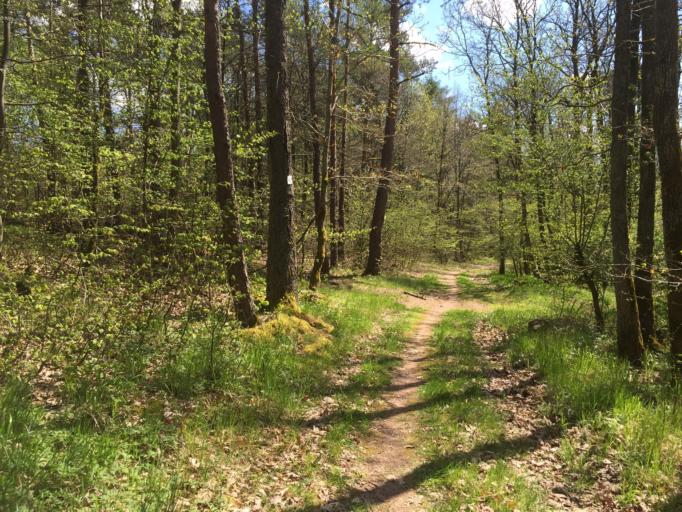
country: DE
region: Bavaria
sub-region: Regierungsbezirk Unterfranken
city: Sulzfeld
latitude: 50.2550
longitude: 10.4510
